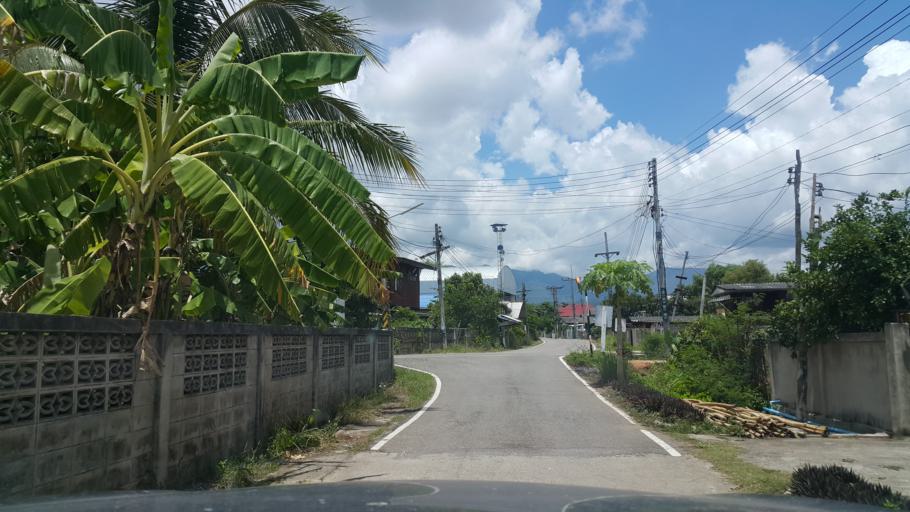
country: TH
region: Phayao
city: Phayao
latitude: 19.1884
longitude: 99.8235
